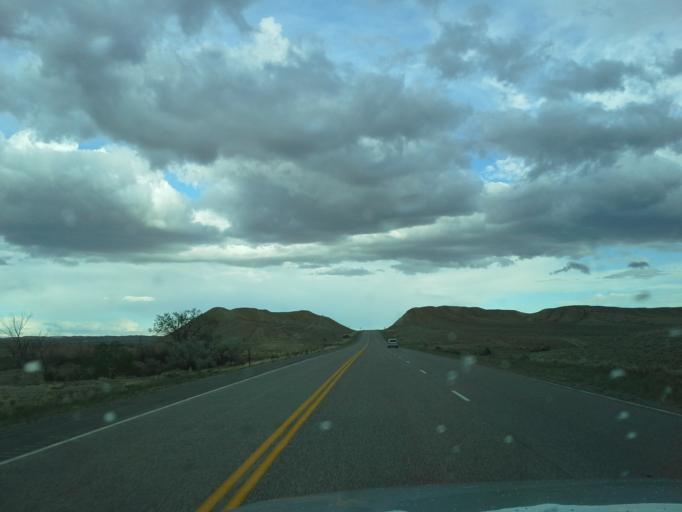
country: US
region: Wyoming
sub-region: Big Horn County
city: Lovell
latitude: 44.7916
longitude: -108.3666
